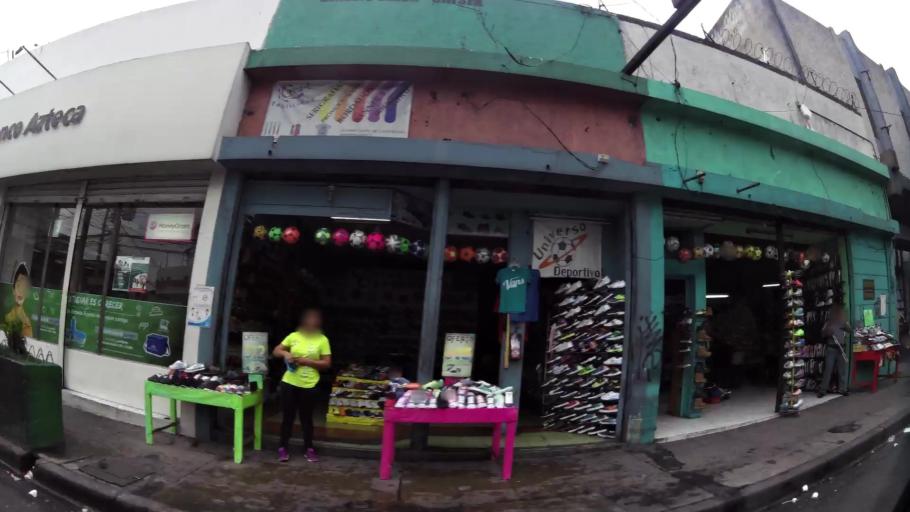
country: SV
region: San Salvador
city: San Salvador
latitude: 13.7001
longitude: -89.1935
